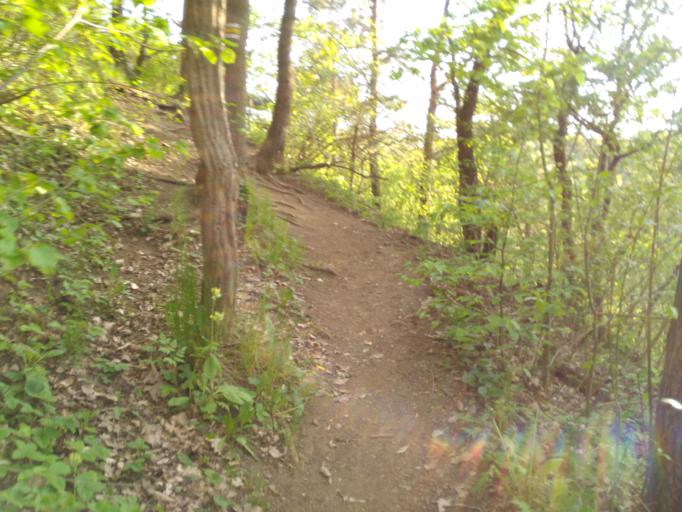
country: CZ
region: Central Bohemia
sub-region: Okres Beroun
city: Kraluv Dvur
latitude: 49.9197
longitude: 14.0468
